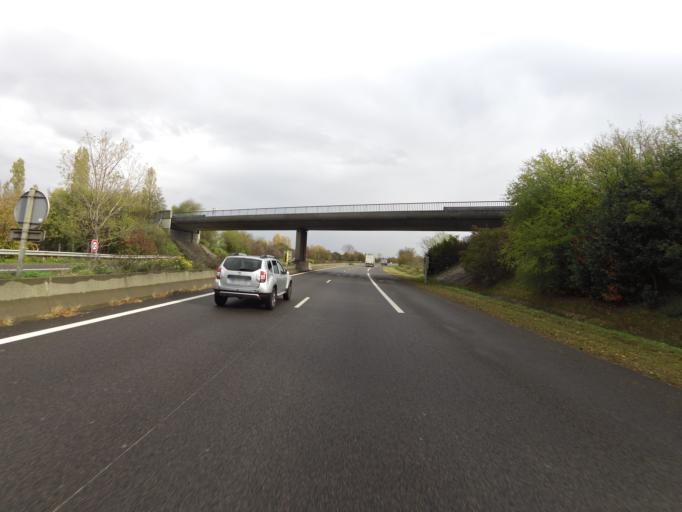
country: FR
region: Rhone-Alpes
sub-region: Departement du Rhone
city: Corbas
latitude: 45.6417
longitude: 4.8987
